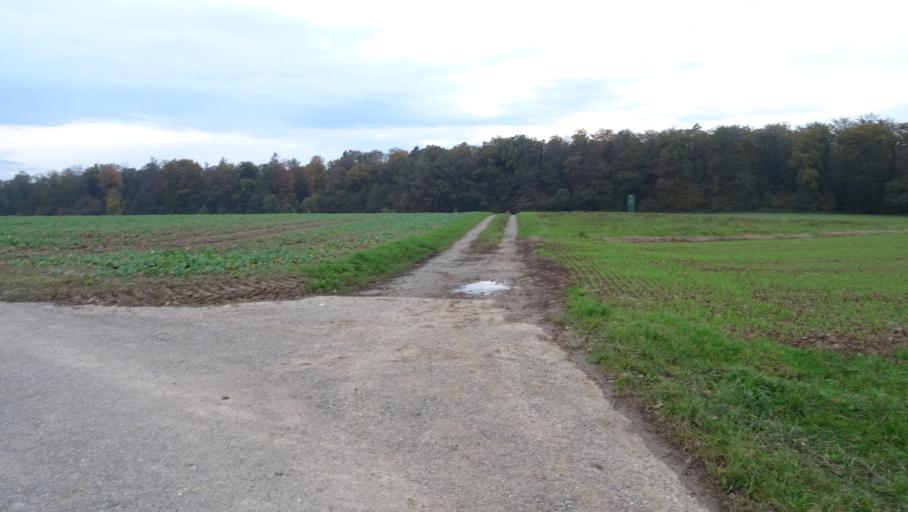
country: DE
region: Baden-Wuerttemberg
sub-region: Karlsruhe Region
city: Binau
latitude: 49.3758
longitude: 9.0776
